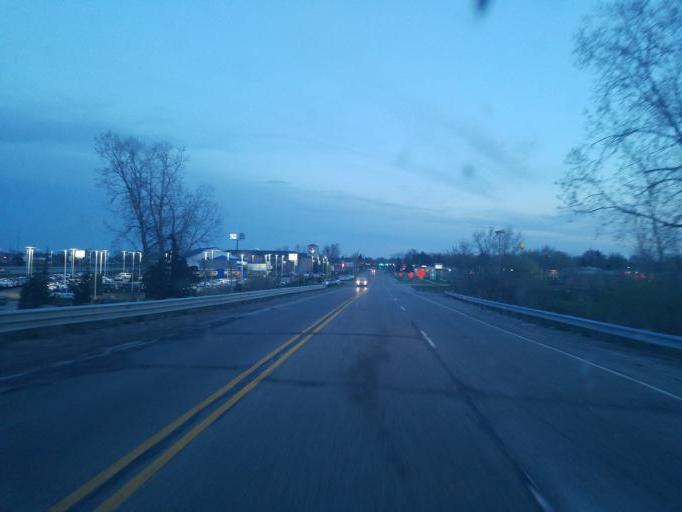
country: US
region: Michigan
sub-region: Washtenaw County
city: Milan
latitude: 42.0994
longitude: -83.6767
